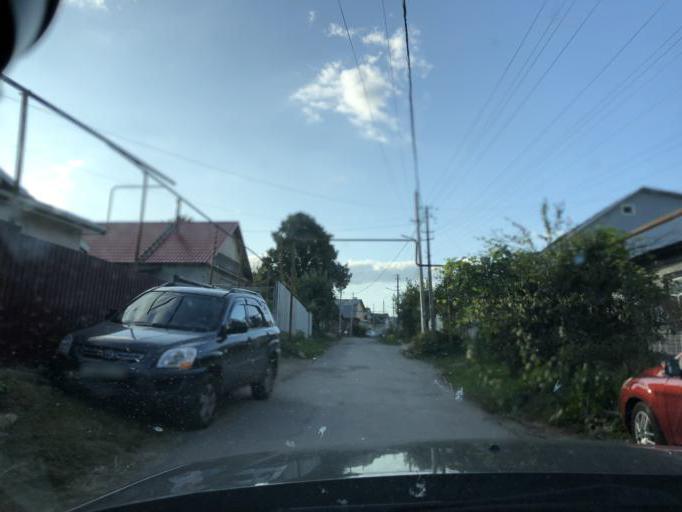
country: RU
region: Tula
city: Kosaya Gora
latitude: 54.1814
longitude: 37.5381
